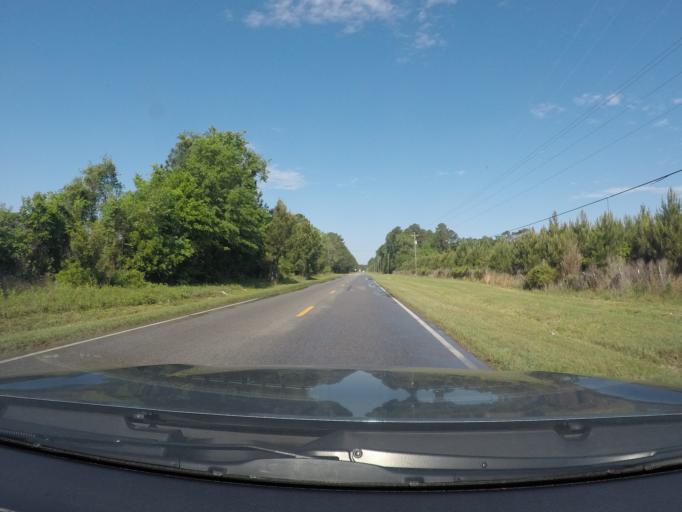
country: US
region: Georgia
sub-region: Chatham County
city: Bloomingdale
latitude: 32.0552
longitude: -81.2974
